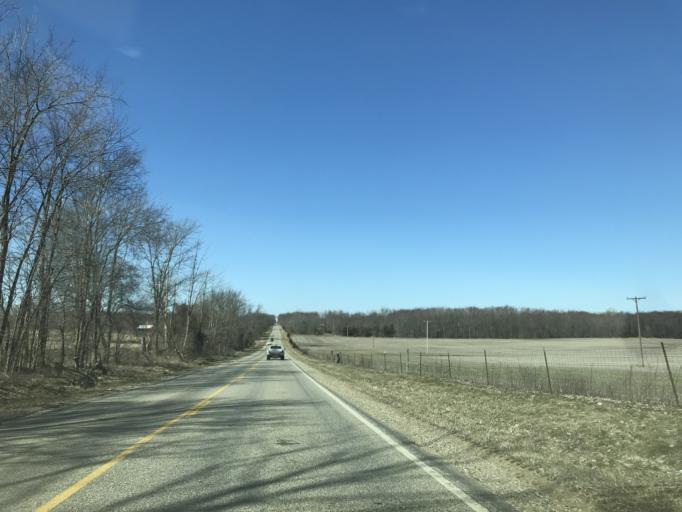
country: US
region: Michigan
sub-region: Hillsdale County
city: Litchfield
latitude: 41.9857
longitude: -84.8012
